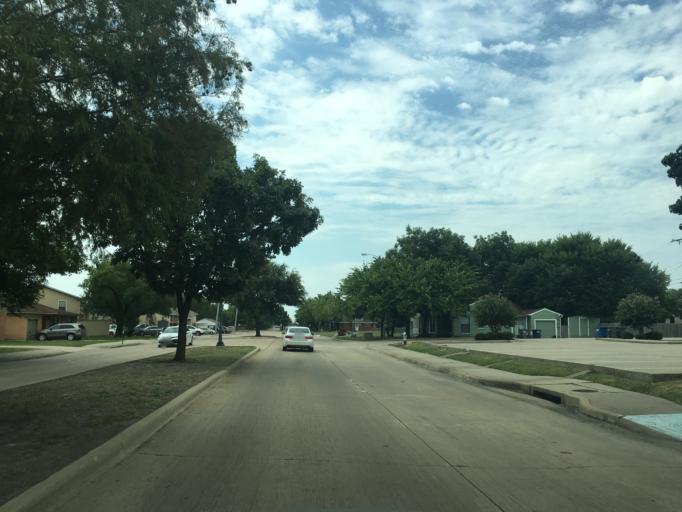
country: US
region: Texas
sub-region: Collin County
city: Wylie
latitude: 33.0112
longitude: -96.5390
